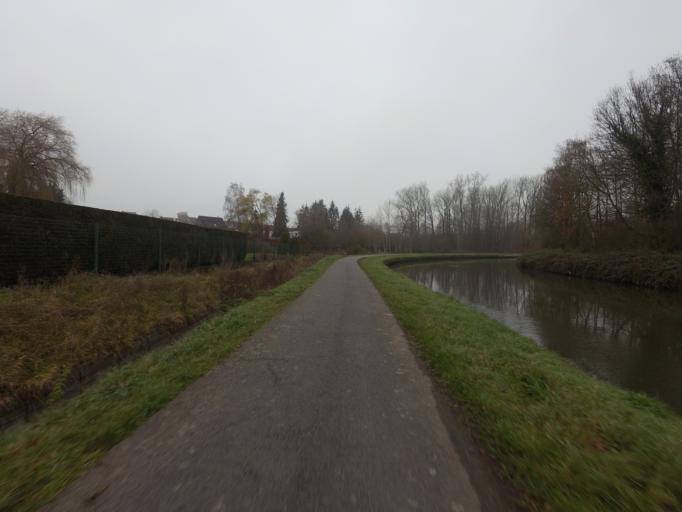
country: BE
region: Flanders
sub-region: Provincie Oost-Vlaanderen
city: Geraardsbergen
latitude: 50.7631
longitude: 3.8688
